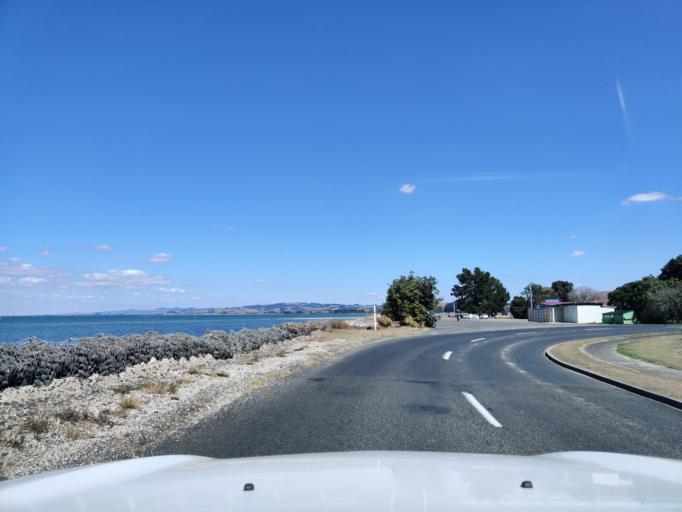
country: NZ
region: Waikato
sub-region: Thames-Coromandel District
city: Thames
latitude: -37.1087
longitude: 175.2990
